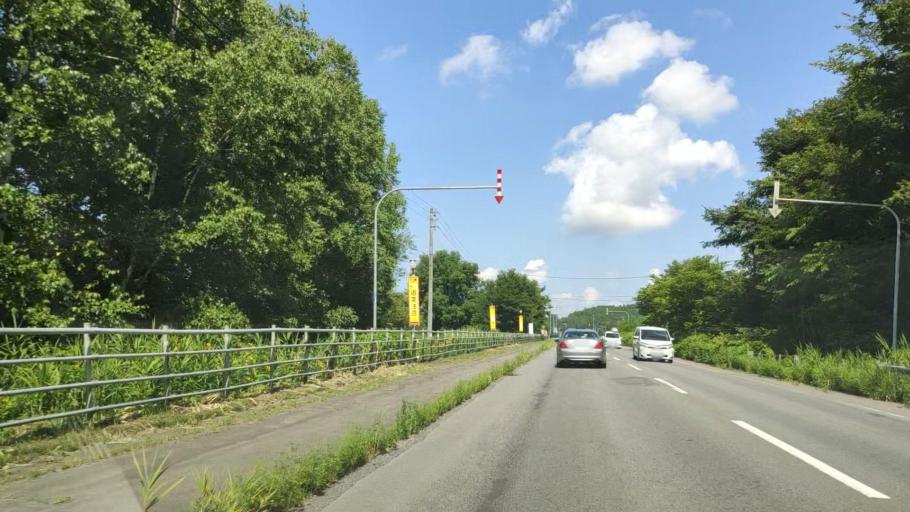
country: JP
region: Hokkaido
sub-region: Asahikawa-shi
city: Asahikawa
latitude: 43.6233
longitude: 142.4679
